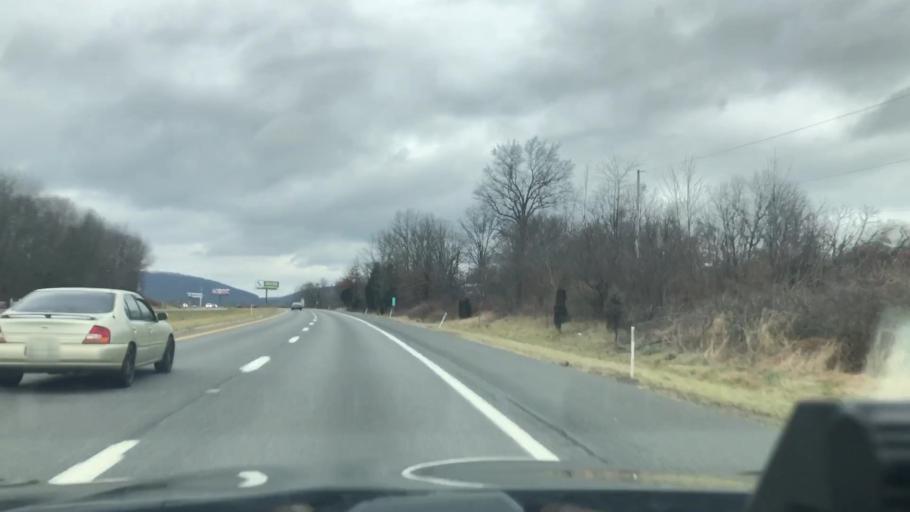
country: US
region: Pennsylvania
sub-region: Northampton County
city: Wind Gap
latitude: 40.8208
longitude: -75.2974
